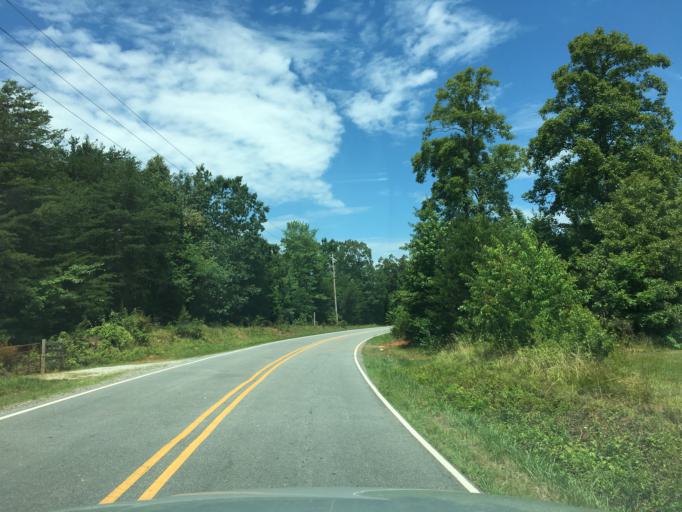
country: US
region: North Carolina
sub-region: Burke County
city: Glen Alpine
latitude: 35.6372
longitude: -81.7947
